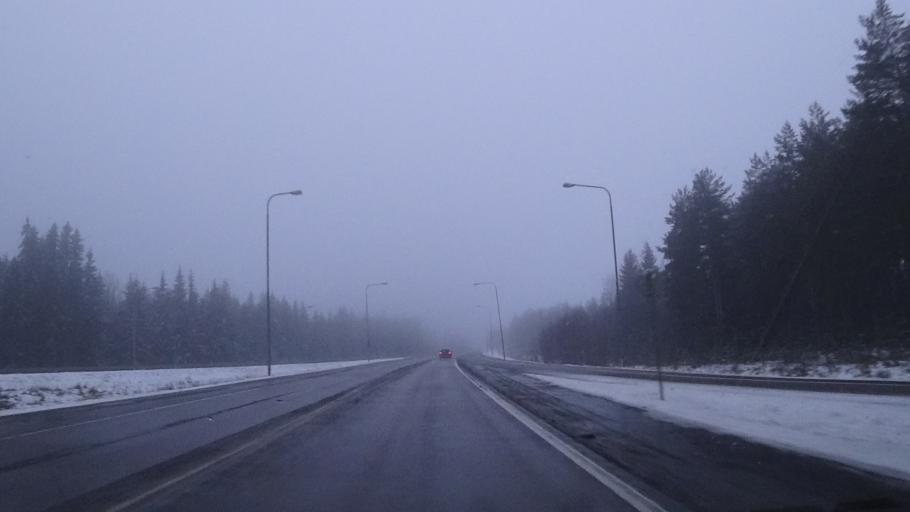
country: FI
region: Paijanne Tavastia
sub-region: Lahti
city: Hollola
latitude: 60.9838
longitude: 25.4157
